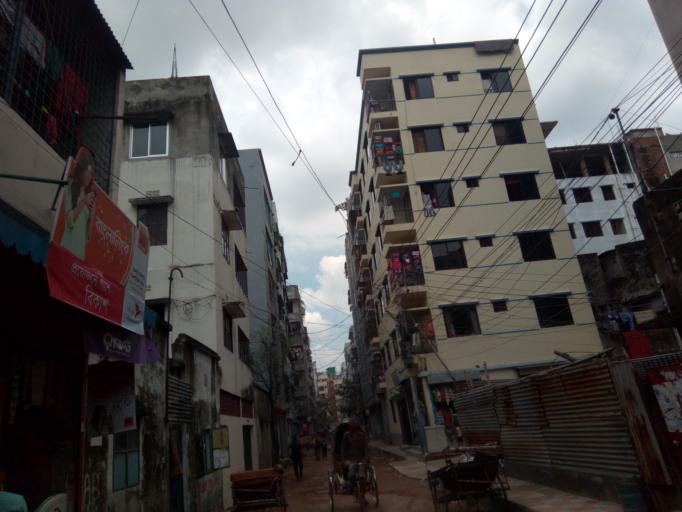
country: BD
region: Dhaka
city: Azimpur
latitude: 23.7683
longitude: 90.3587
